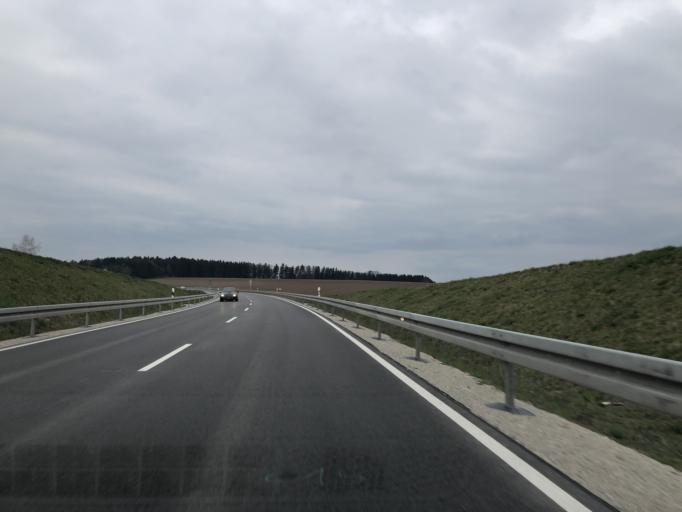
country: DE
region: Bavaria
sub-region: Upper Bavaria
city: Zolling
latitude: 48.4284
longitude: 11.7748
